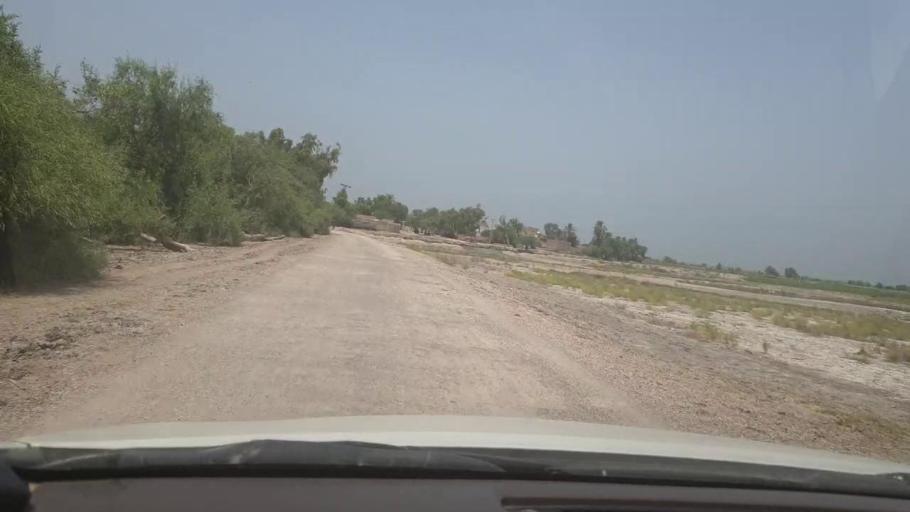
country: PK
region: Sindh
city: Shikarpur
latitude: 27.9469
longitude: 68.5718
